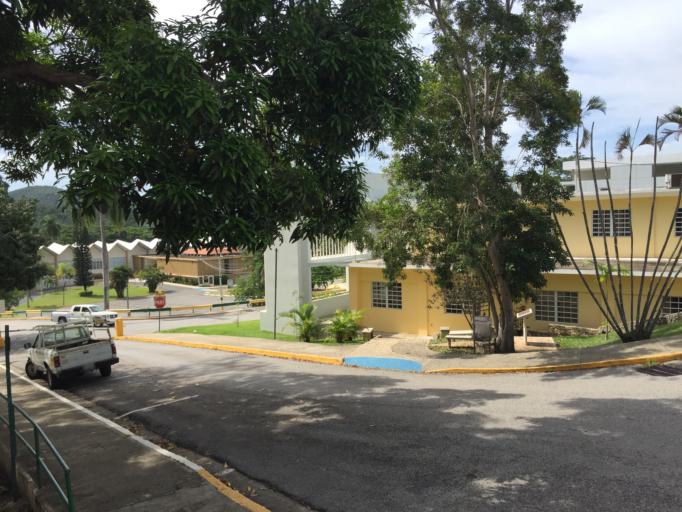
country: PR
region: San German
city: San German
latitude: 18.0841
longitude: -67.0491
